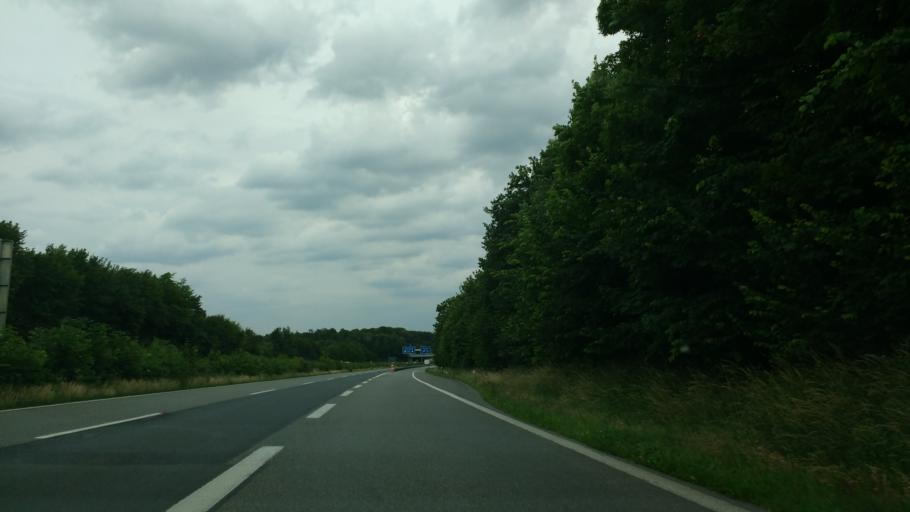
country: DE
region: North Rhine-Westphalia
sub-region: Regierungsbezirk Detmold
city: Wunnenberg
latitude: 51.5770
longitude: 8.7158
